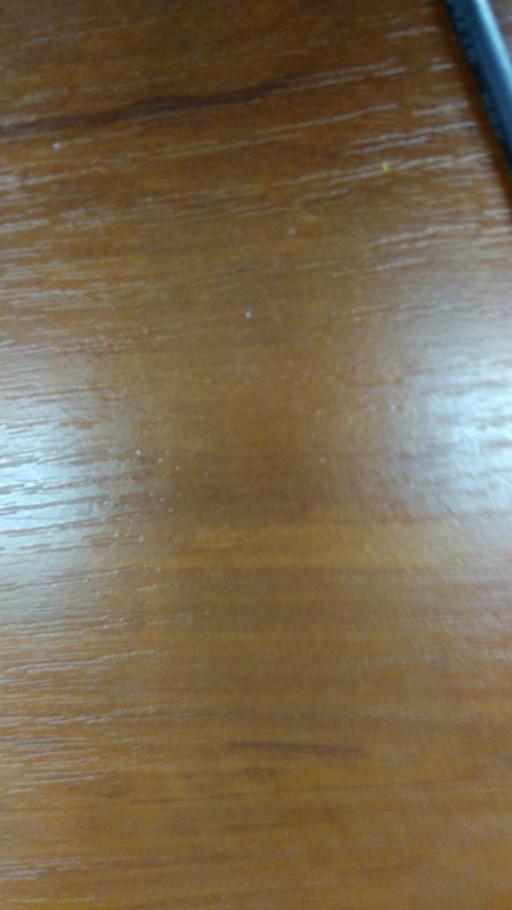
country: RU
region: Tverskaya
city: Emmaus
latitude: 56.7814
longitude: 36.1035
